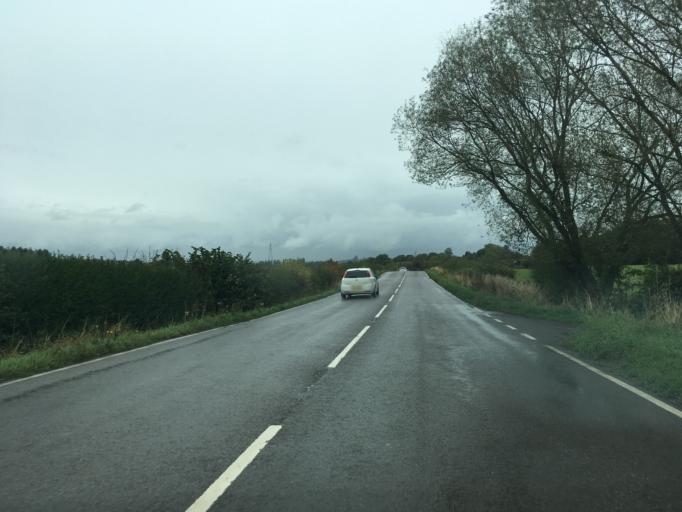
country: GB
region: England
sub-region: Nottinghamshire
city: East Leake
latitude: 52.8475
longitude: -1.1823
